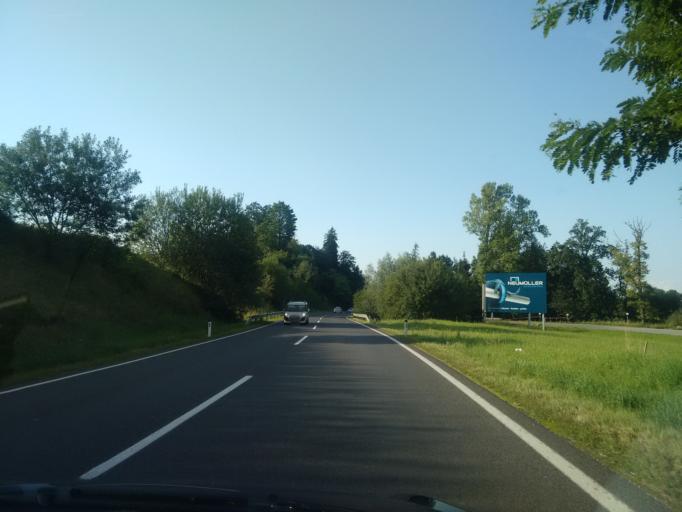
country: AT
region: Upper Austria
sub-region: Politischer Bezirk Braunau am Inn
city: Altheim
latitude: 48.2527
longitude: 13.2122
